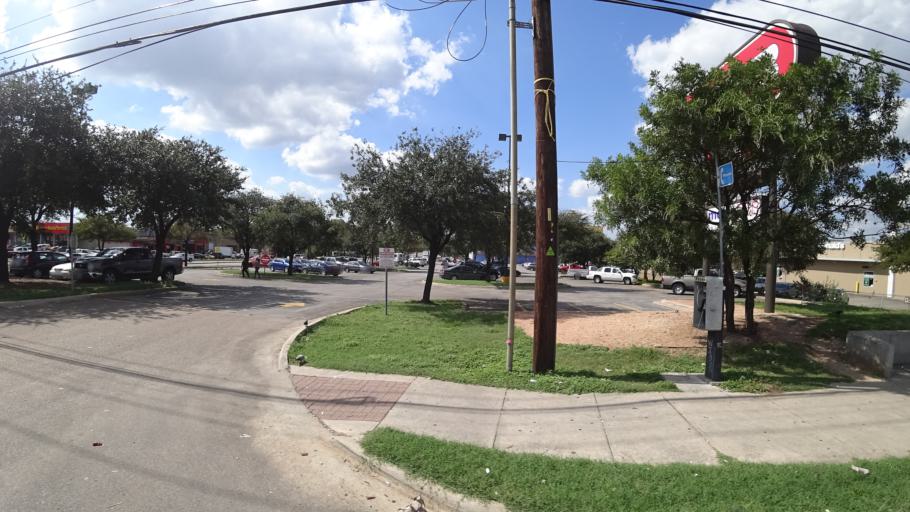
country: US
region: Texas
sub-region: Travis County
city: Wells Branch
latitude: 30.3637
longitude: -97.6968
